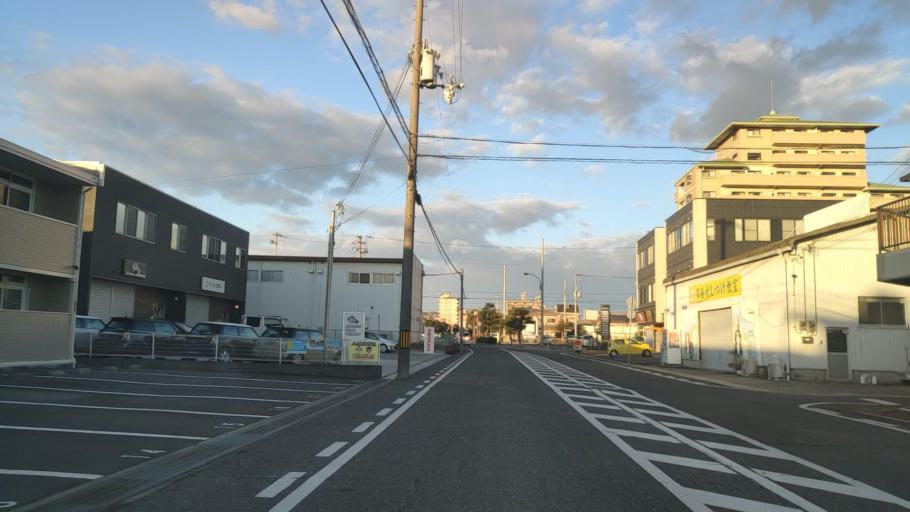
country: JP
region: Hyogo
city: Himeji
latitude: 34.8134
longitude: 134.6890
